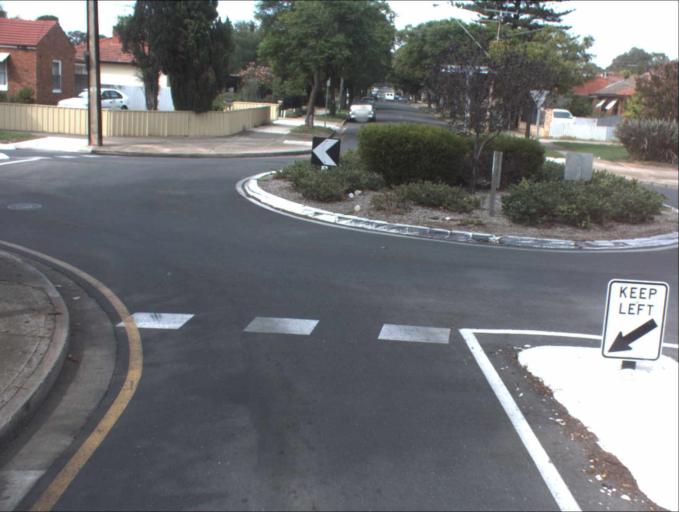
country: AU
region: South Australia
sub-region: Port Adelaide Enfield
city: Blair Athol
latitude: -34.8561
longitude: 138.5957
